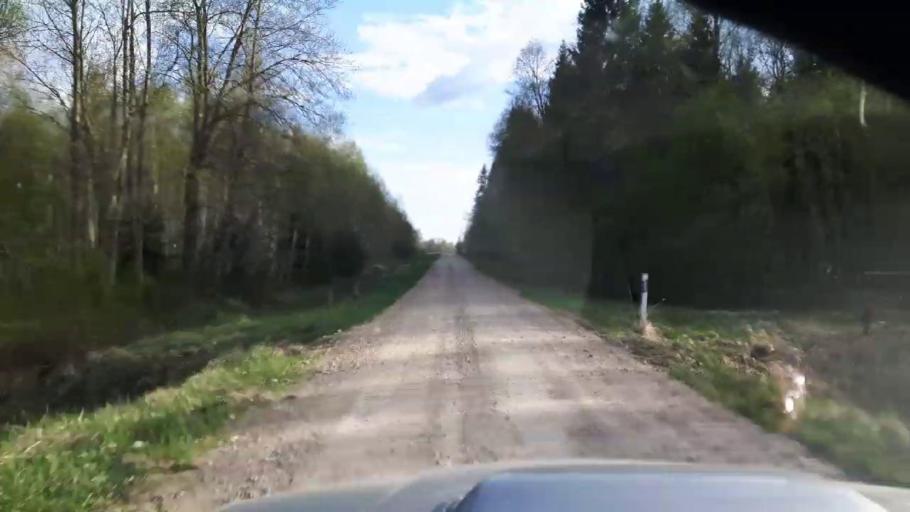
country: EE
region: Paernumaa
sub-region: Tootsi vald
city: Tootsi
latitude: 58.4422
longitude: 24.8121
